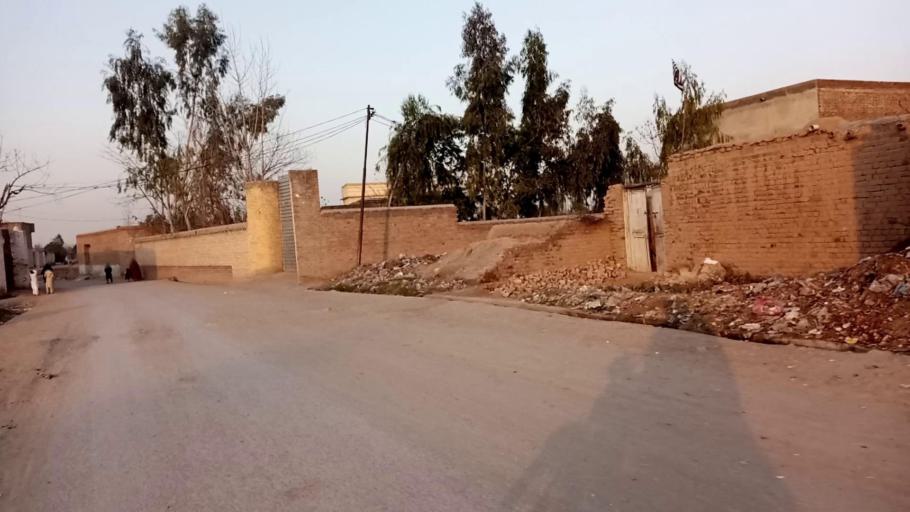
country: PK
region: Khyber Pakhtunkhwa
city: Peshawar
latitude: 34.0448
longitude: 71.4529
